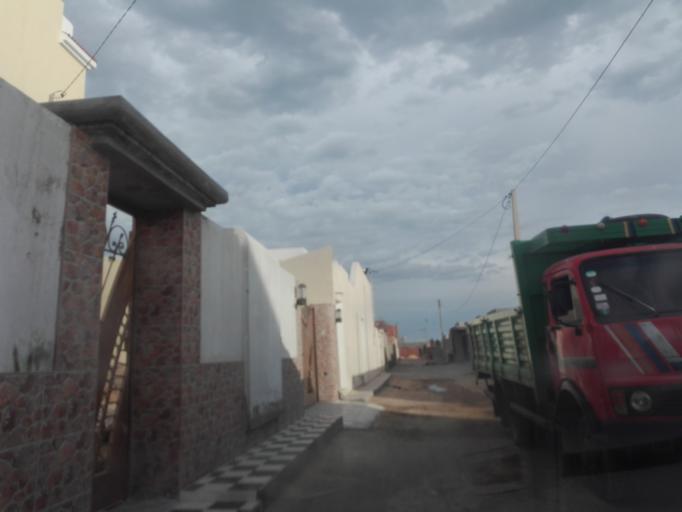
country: TN
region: Safaqis
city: Al Qarmadah
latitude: 34.8072
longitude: 10.8609
